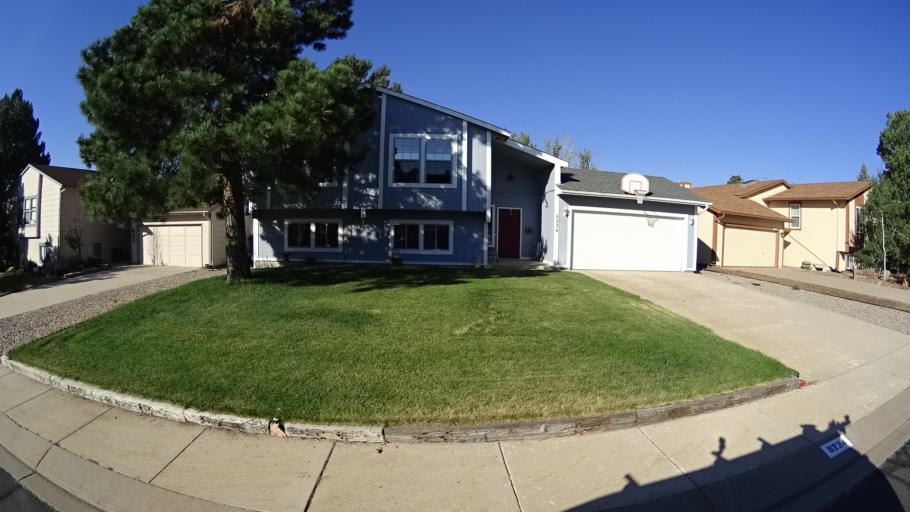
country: US
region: Colorado
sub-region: El Paso County
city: Black Forest
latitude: 38.9521
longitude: -104.7692
